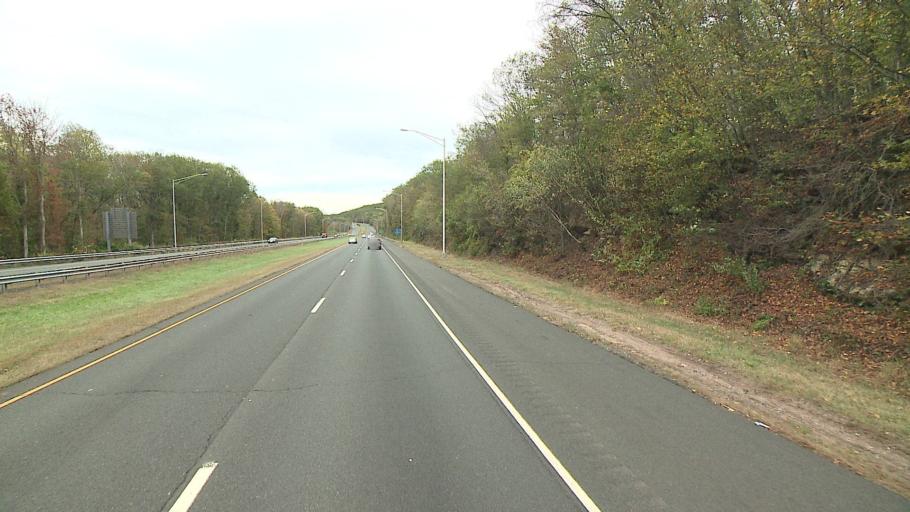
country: US
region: Connecticut
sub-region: Middlesex County
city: Higganum
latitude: 41.5207
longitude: -72.6055
